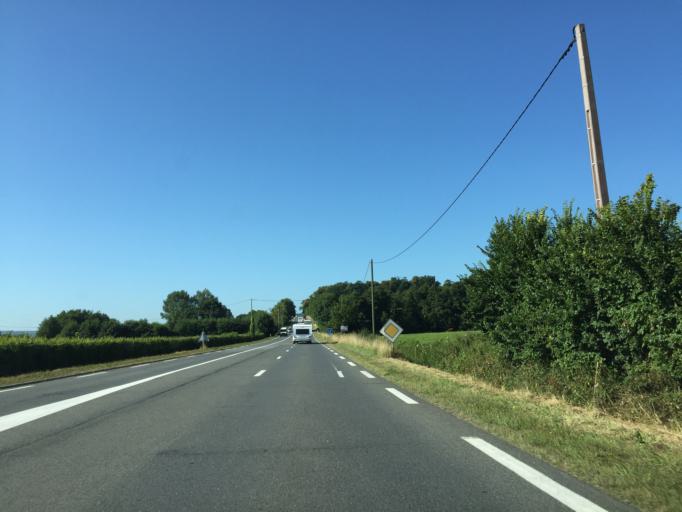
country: FR
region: Lower Normandy
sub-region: Departement du Calvados
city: Saint-Gatien-des-Bois
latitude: 49.2697
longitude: 0.2178
